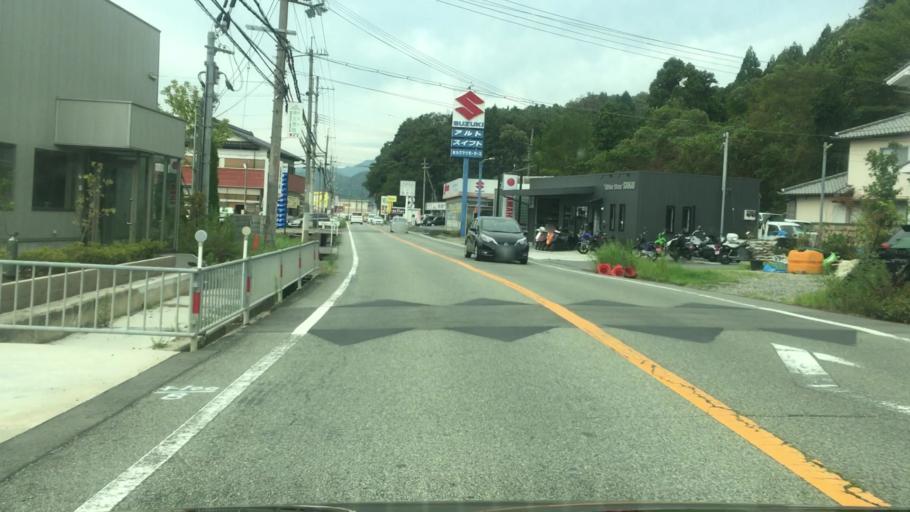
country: JP
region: Hyogo
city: Sasayama
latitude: 35.0659
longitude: 135.1936
